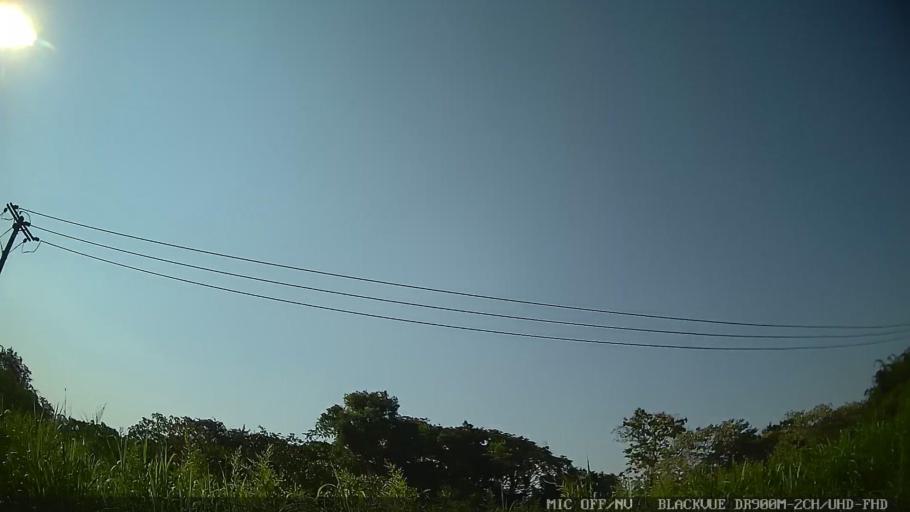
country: BR
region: Sao Paulo
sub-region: Itatiba
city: Itatiba
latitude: -22.9833
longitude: -46.8369
